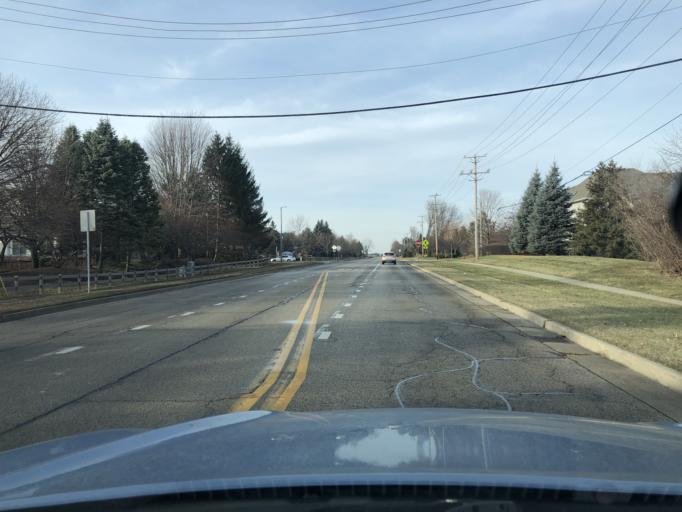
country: US
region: Illinois
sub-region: McHenry County
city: Lake in the Hills
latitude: 42.1539
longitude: -88.3258
